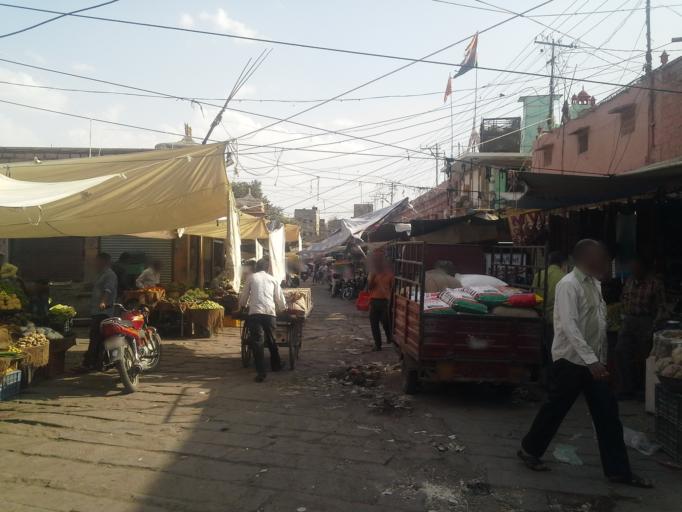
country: IN
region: Rajasthan
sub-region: Jodhpur
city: Jodhpur
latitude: 26.2955
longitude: 73.0233
